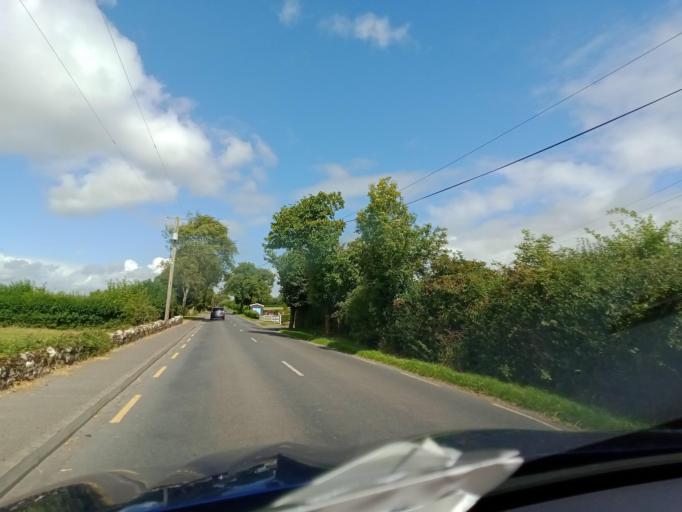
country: IE
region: Leinster
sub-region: Laois
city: Abbeyleix
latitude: 52.9520
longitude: -7.3031
